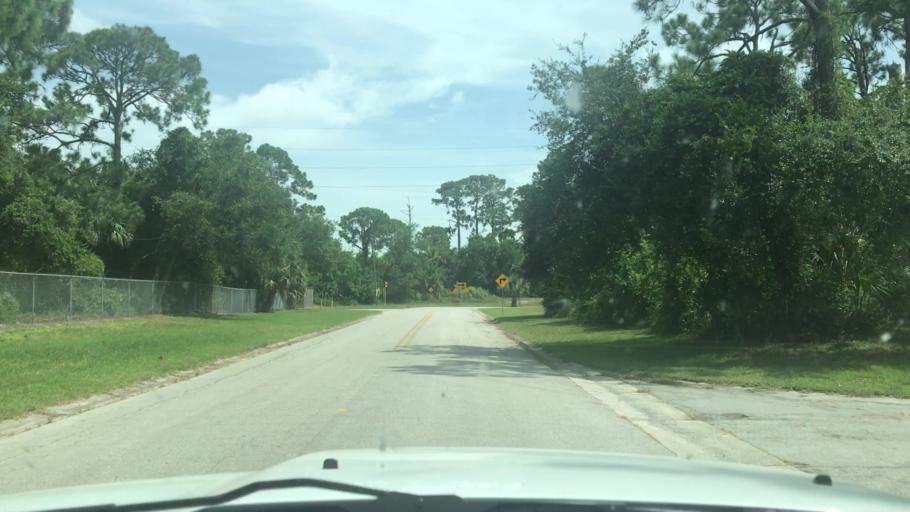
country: US
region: Florida
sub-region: Indian River County
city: Florida Ridge
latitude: 27.5588
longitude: -80.3818
